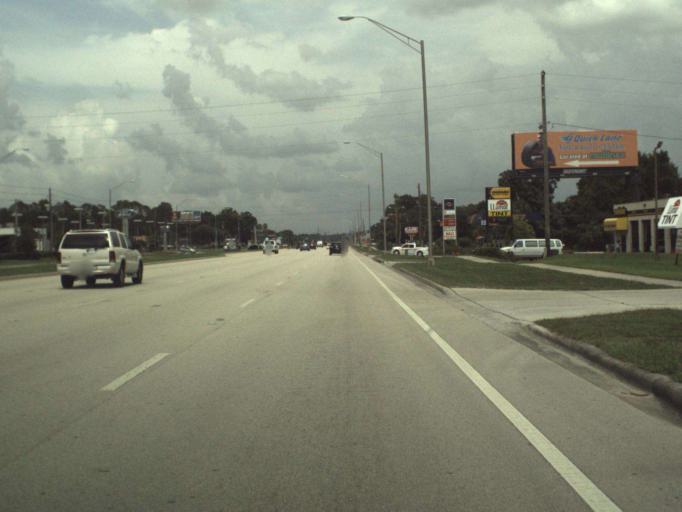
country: US
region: Florida
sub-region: Orange County
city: South Apopka
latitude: 28.6728
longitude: -81.4842
